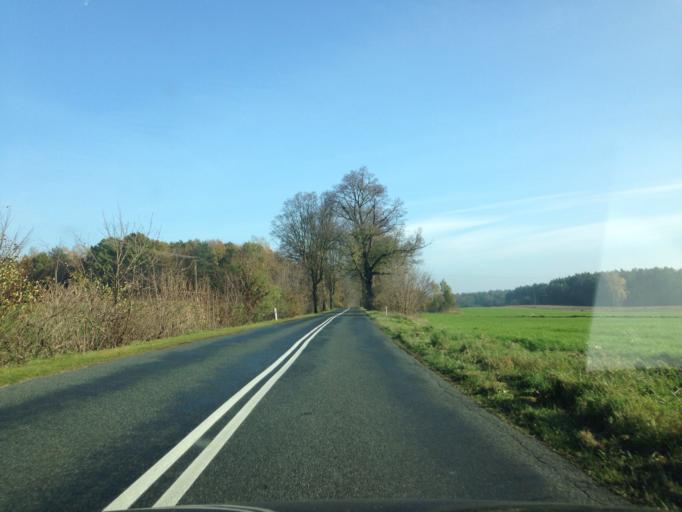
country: PL
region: Kujawsko-Pomorskie
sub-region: Powiat brodnicki
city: Gorzno
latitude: 53.2451
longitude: 19.6541
